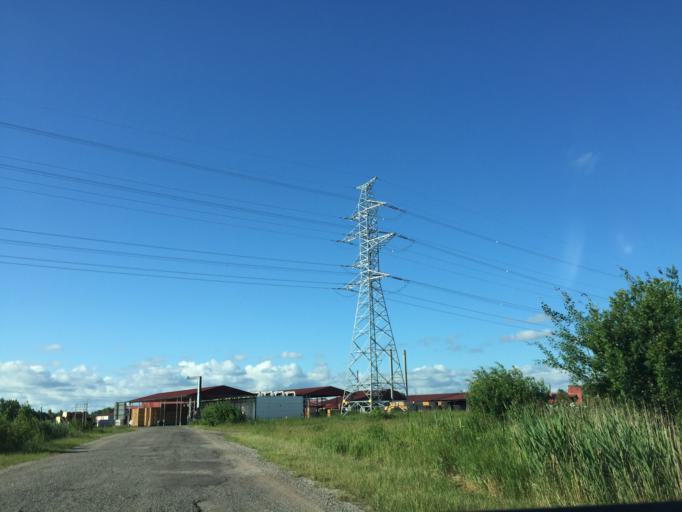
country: LV
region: Ventspils
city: Ventspils
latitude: 57.3986
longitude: 21.6494
